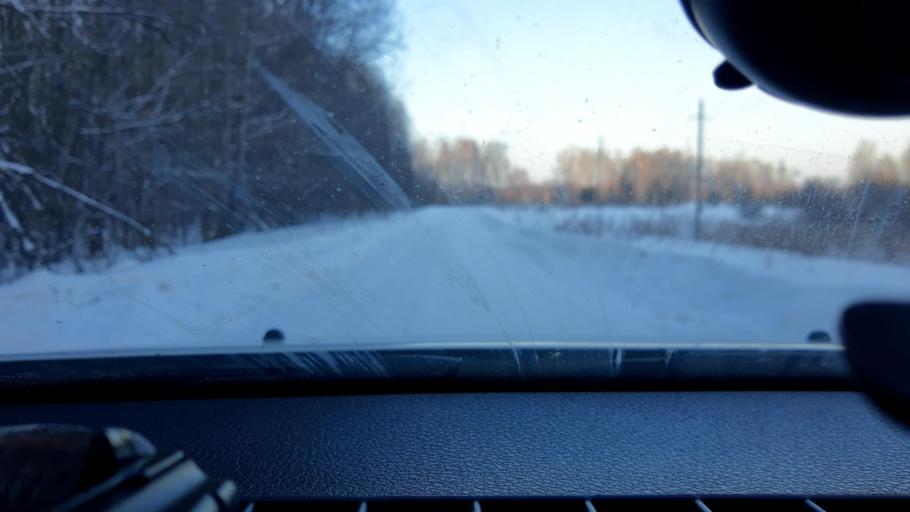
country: RU
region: Bashkortostan
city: Kudeyevskiy
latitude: 54.8008
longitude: 56.6762
